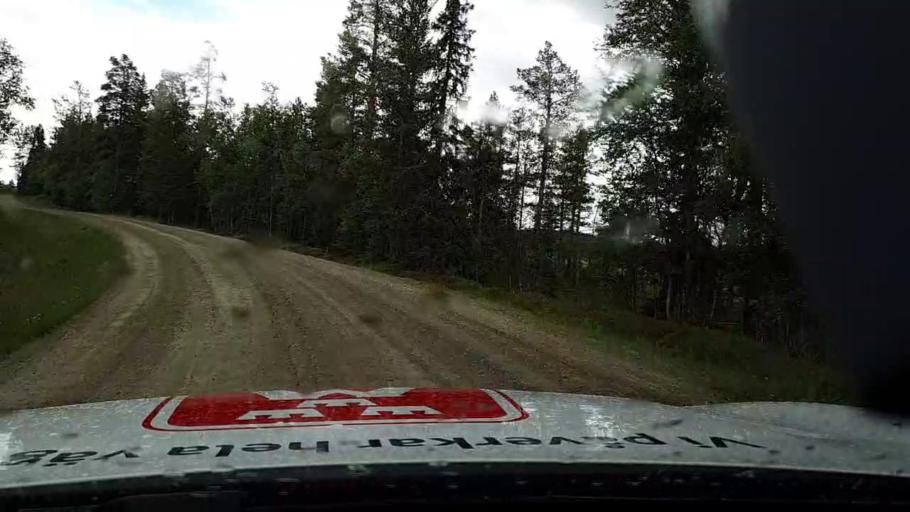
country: SE
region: Jaemtland
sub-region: Are Kommun
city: Jarpen
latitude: 62.6132
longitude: 13.1989
